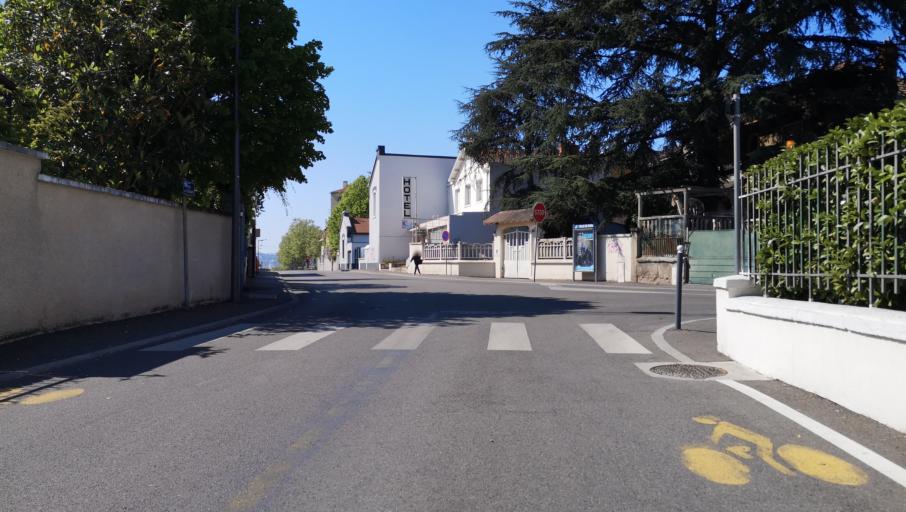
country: FR
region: Rhone-Alpes
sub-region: Departement du Rhone
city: Bron
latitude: 45.7347
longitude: 4.8917
